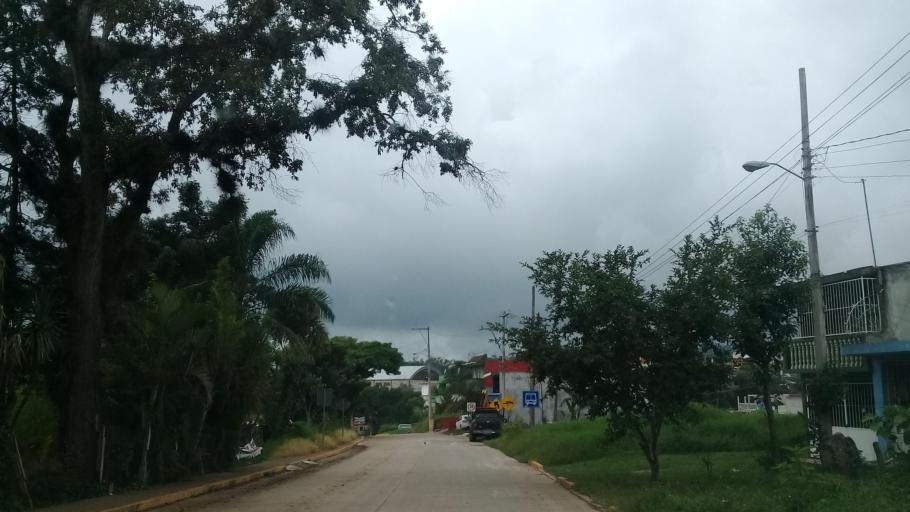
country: MX
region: Veracruz
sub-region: Emiliano Zapata
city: Las Trancas
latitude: 19.5025
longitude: -96.8698
